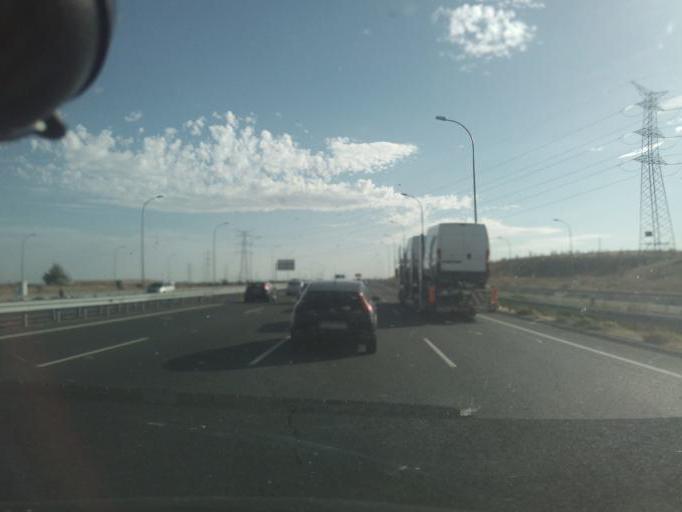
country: ES
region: Madrid
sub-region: Provincia de Madrid
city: Villaverde
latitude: 40.2974
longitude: -3.6683
